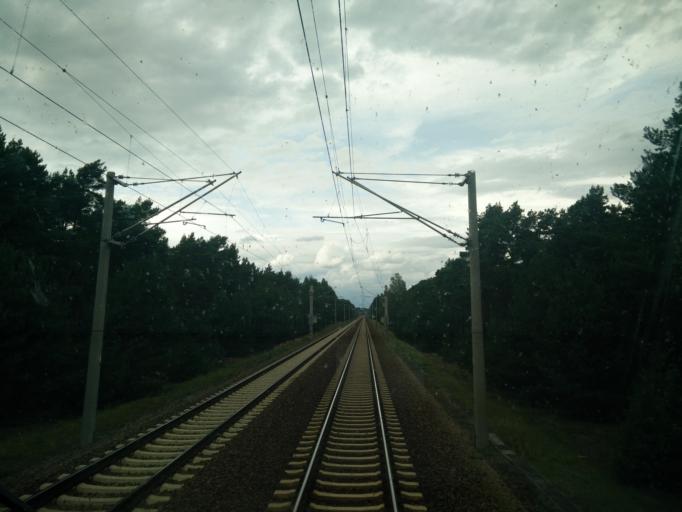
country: DE
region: Brandenburg
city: Kasel-Golzig
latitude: 52.0137
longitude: 13.7427
